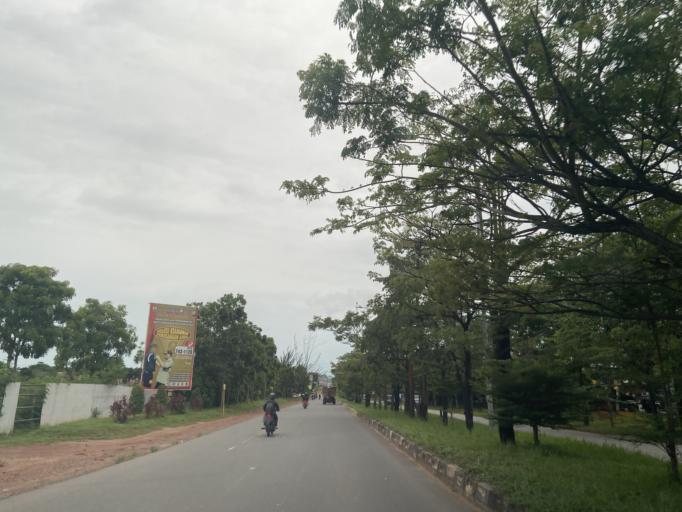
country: SG
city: Singapore
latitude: 1.1208
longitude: 104.0578
